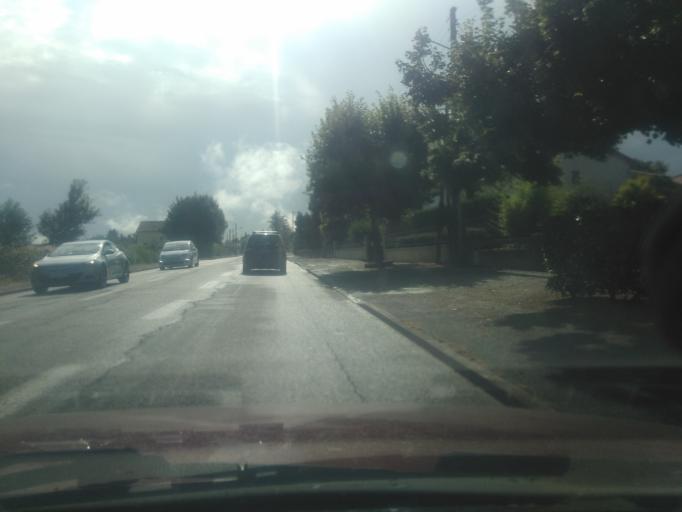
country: FR
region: Poitou-Charentes
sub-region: Departement des Deux-Sevres
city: Parthenay
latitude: 46.6343
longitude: -0.2532
